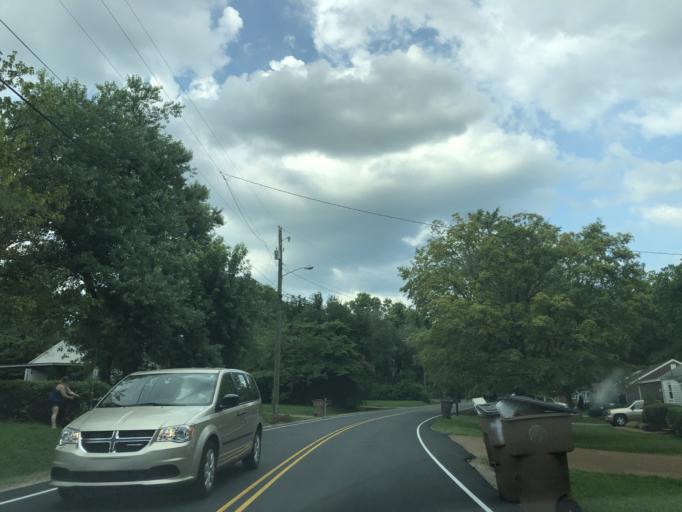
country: US
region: Tennessee
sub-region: Davidson County
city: Lakewood
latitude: 36.1661
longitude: -86.6759
